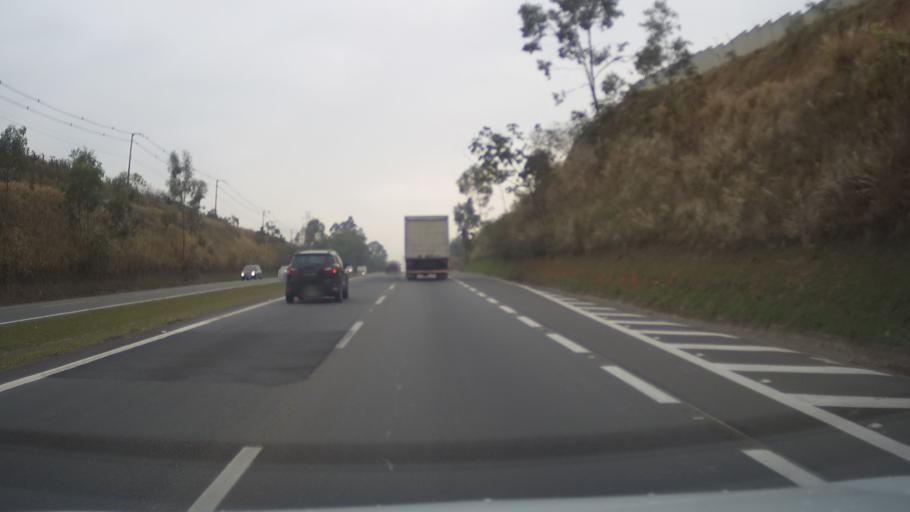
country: BR
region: Sao Paulo
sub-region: Jundiai
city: Jundiai
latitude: -23.1580
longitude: -46.8955
